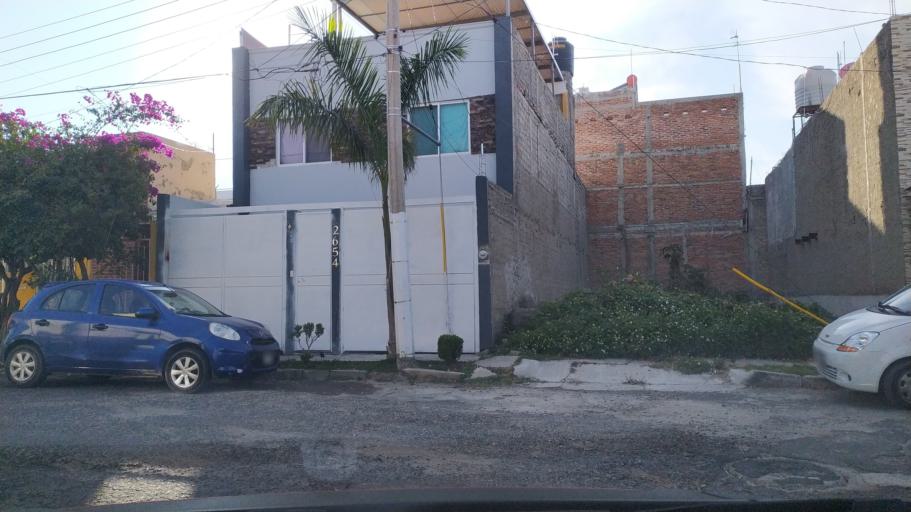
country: MX
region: Jalisco
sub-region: Tlajomulco de Zuniga
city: Palomar
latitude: 20.6277
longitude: -103.4717
